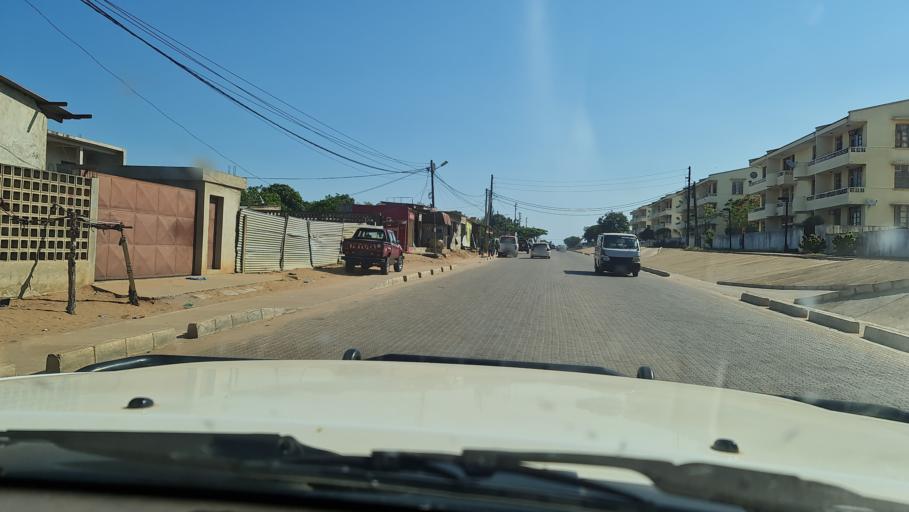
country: MZ
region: Maputo City
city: Maputo
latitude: -25.8385
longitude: 32.6368
